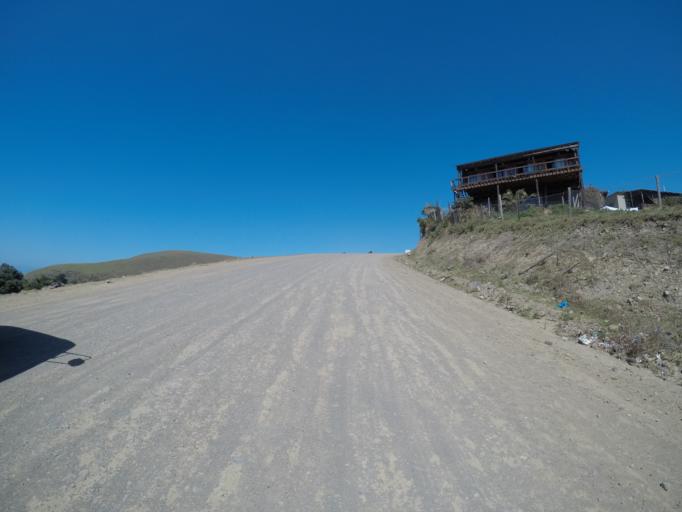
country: ZA
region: Eastern Cape
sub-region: OR Tambo District Municipality
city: Libode
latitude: -31.9868
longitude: 29.1477
